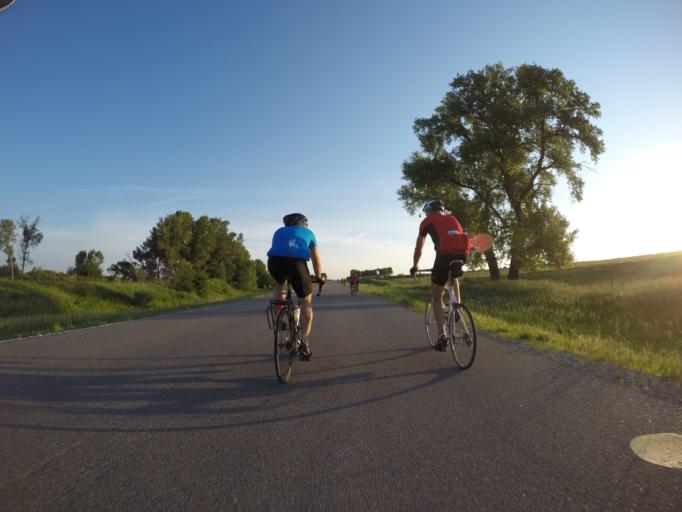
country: US
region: Kansas
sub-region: Marshall County
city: Marysville
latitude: 39.8457
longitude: -96.6009
